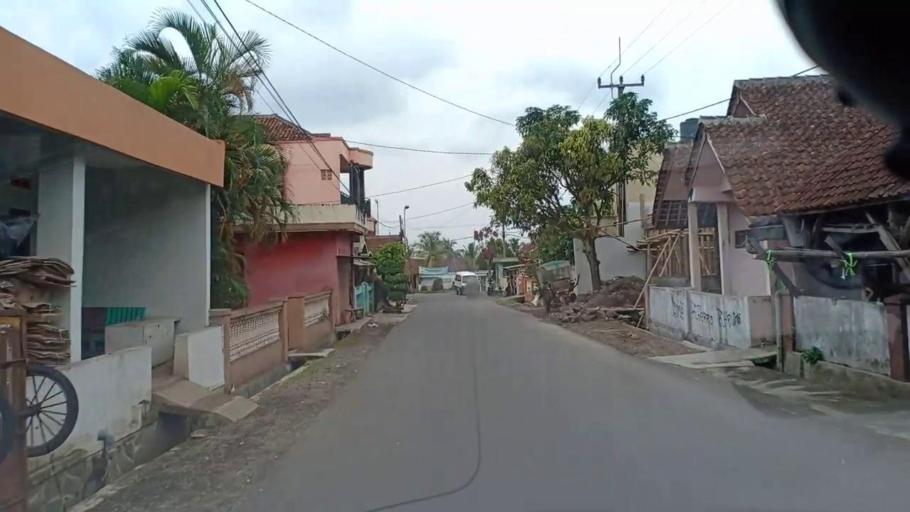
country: ID
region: West Java
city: Lemburwarung
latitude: -7.3378
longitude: 108.2704
